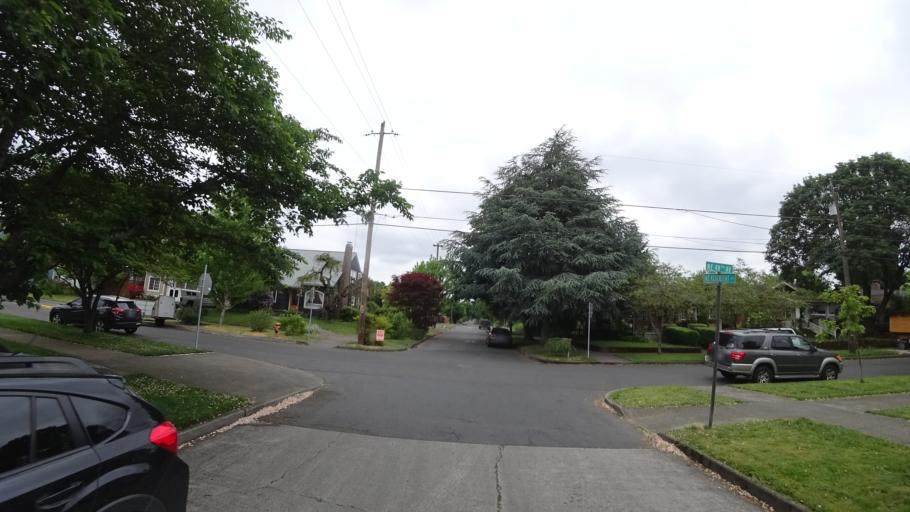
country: US
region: Oregon
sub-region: Multnomah County
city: Portland
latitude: 45.5469
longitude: -122.6139
